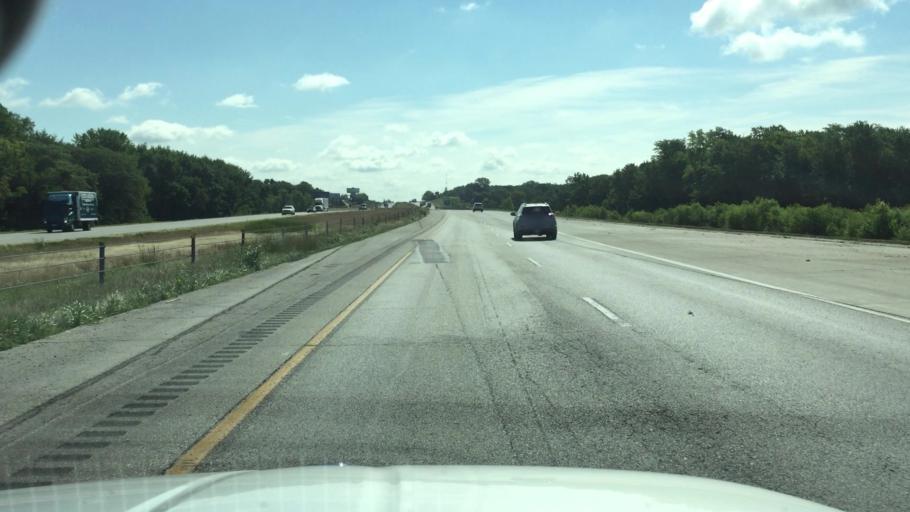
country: US
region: Iowa
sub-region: Cedar County
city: Tipton
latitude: 41.6456
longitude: -91.1399
